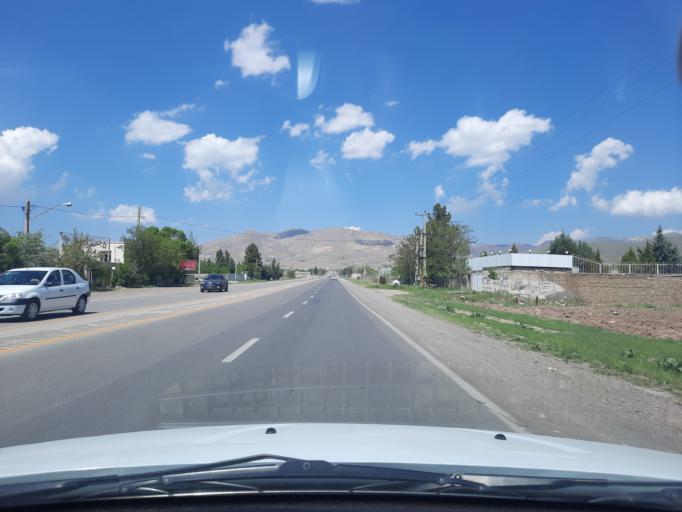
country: IR
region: Qazvin
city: Alvand
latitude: 36.3074
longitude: 50.1447
